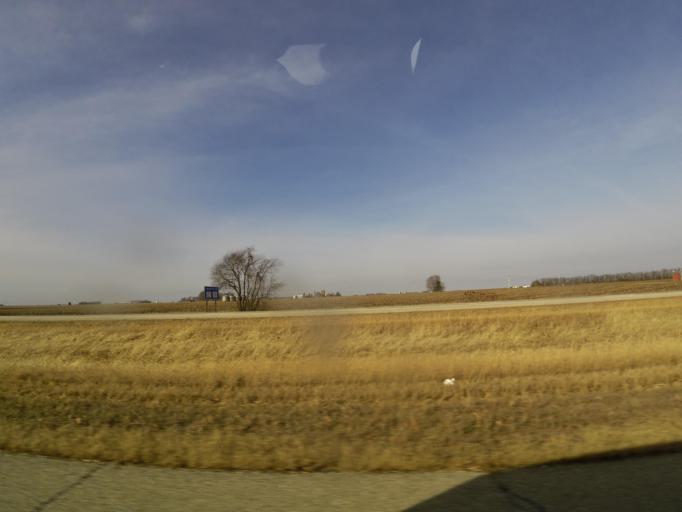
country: US
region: Illinois
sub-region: Macon County
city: Harristown
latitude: 39.8659
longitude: -89.0391
